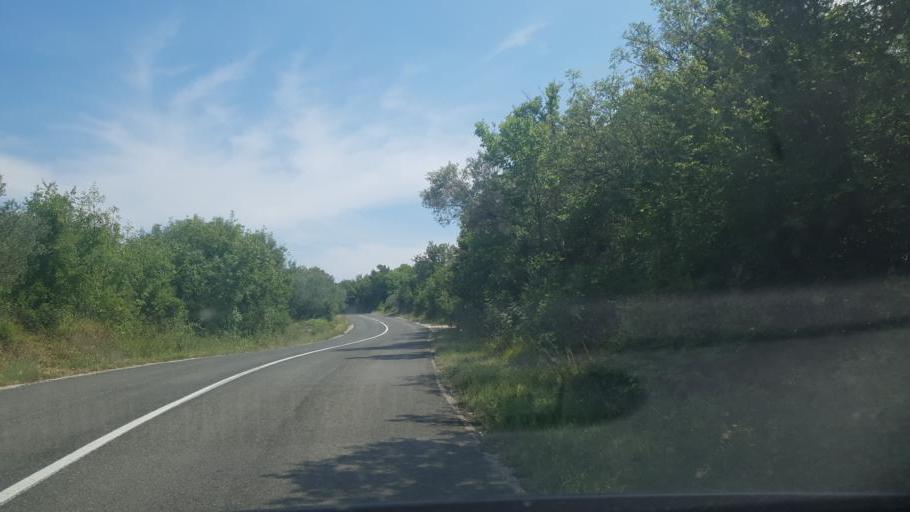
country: HR
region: Primorsko-Goranska
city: Njivice
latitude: 45.1441
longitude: 14.6107
